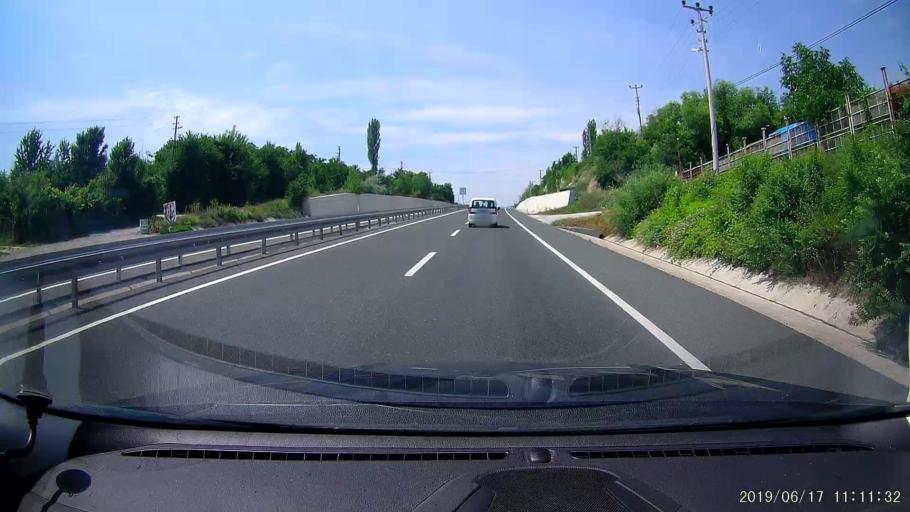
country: TR
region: Kastamonu
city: Tosya
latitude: 40.9852
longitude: 34.0079
